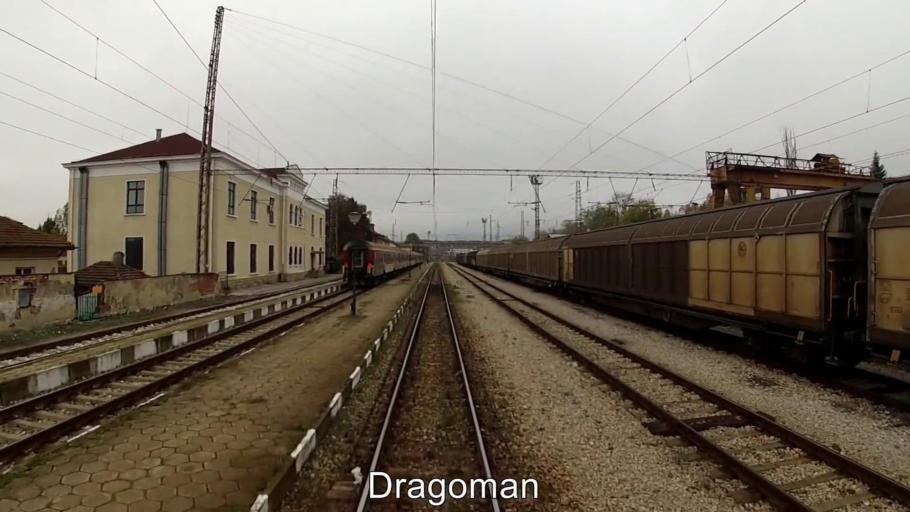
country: BG
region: Sofiya
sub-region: Obshtina Dragoman
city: Dragoman
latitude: 42.9255
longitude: 22.9329
